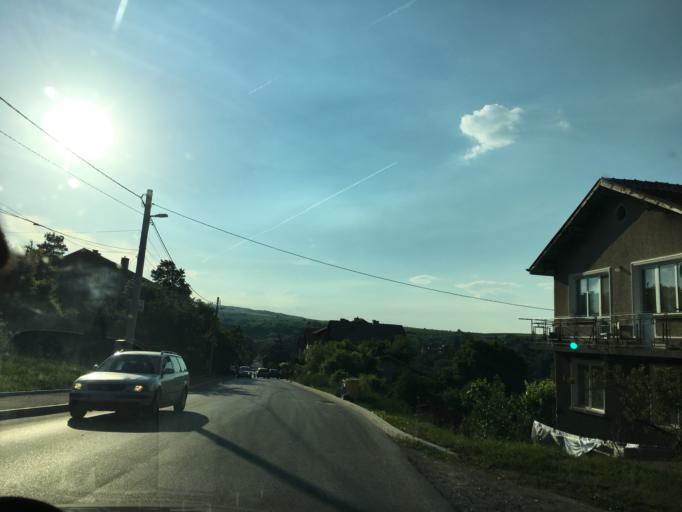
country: BG
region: Sofiya
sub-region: Obshtina Bozhurishte
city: Bozhurishte
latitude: 42.7160
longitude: 23.1387
